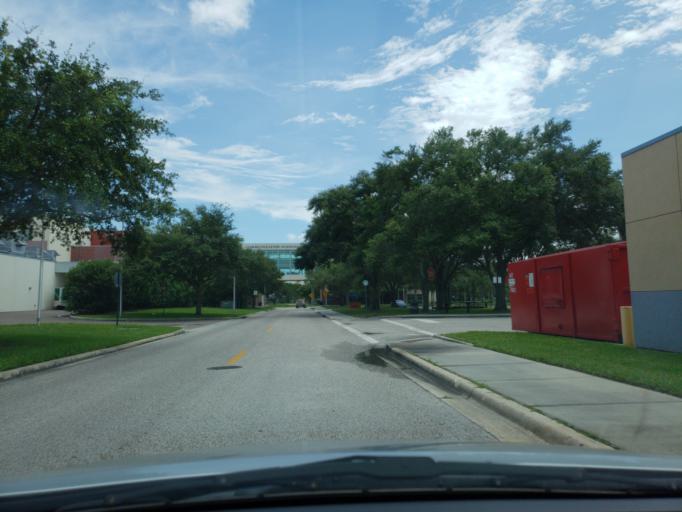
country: US
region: Florida
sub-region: Hillsborough County
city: University
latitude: 28.0652
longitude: -82.4190
